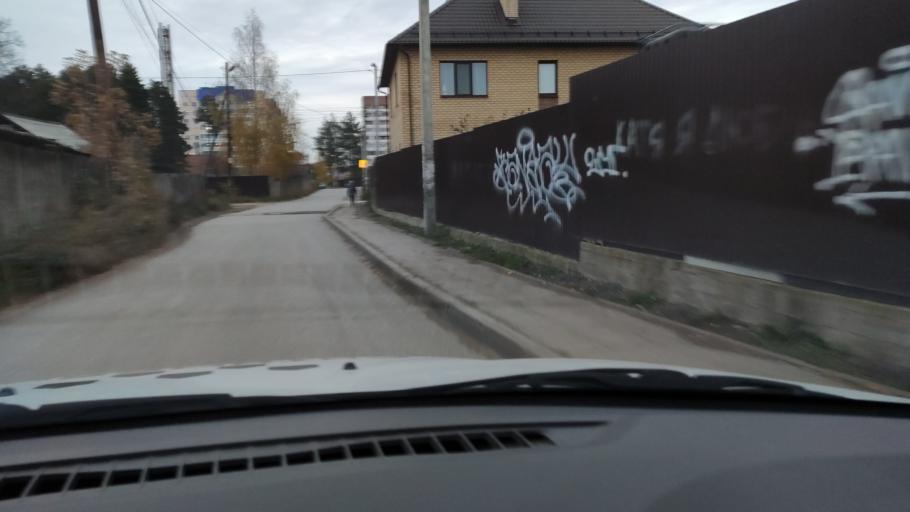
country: RU
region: Perm
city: Kondratovo
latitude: 58.0389
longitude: 56.1165
